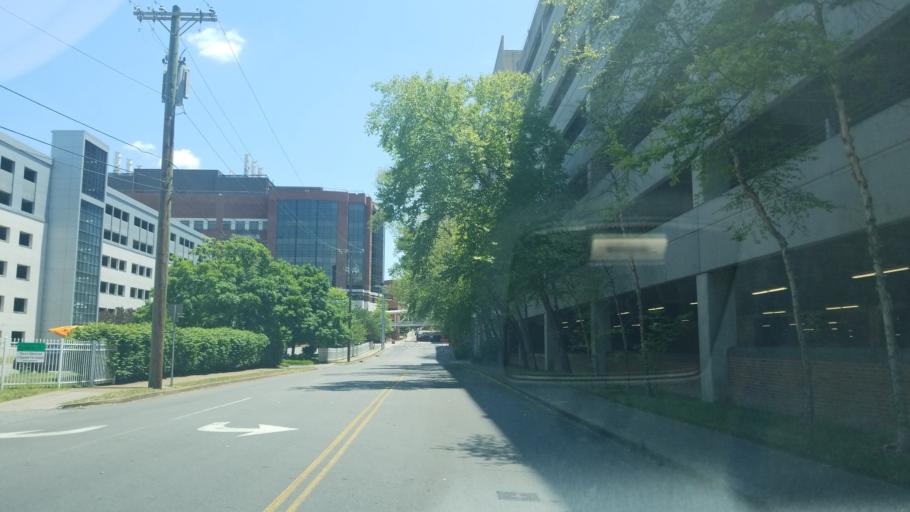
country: US
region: Tennessee
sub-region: Davidson County
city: Nashville
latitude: 36.1400
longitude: -86.8049
